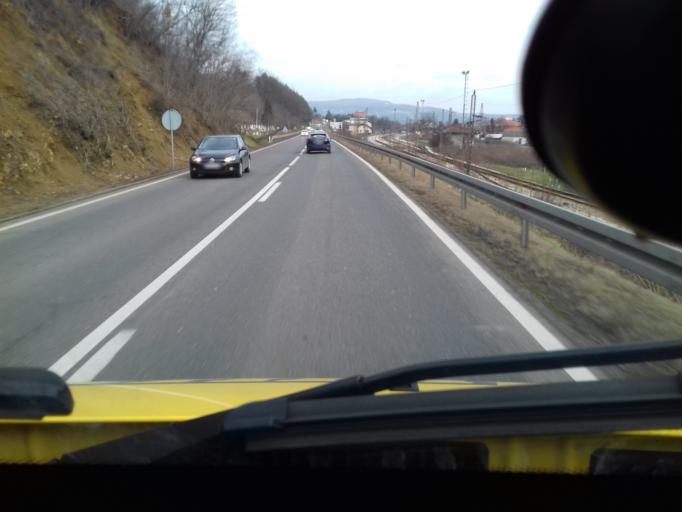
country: BA
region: Federation of Bosnia and Herzegovina
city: Zepce
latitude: 44.4248
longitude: 18.0236
